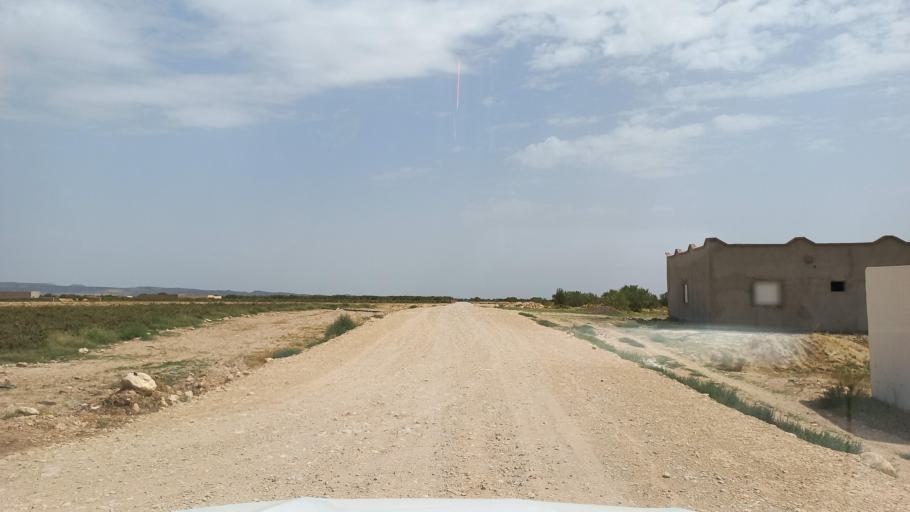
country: TN
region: Al Qasrayn
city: Kasserine
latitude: 35.2811
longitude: 9.0095
